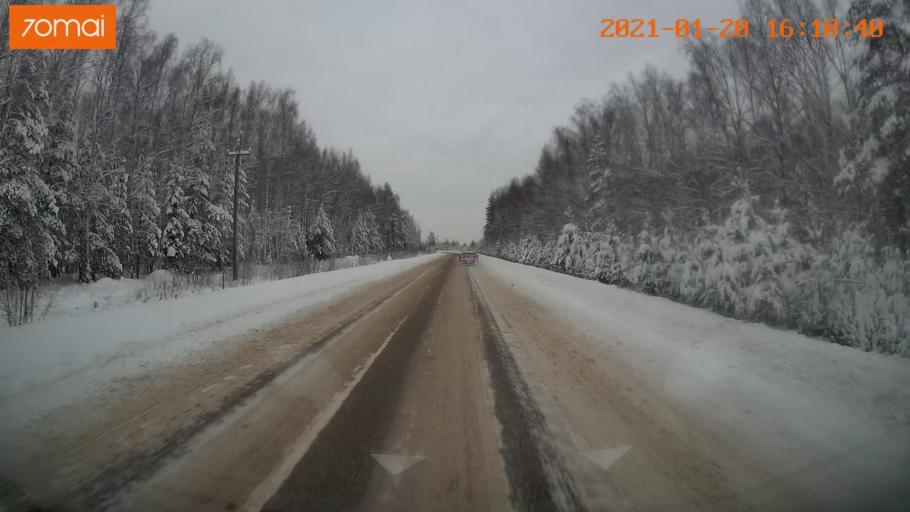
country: RU
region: Vladimir
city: Sudogda
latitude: 56.0943
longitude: 40.7860
